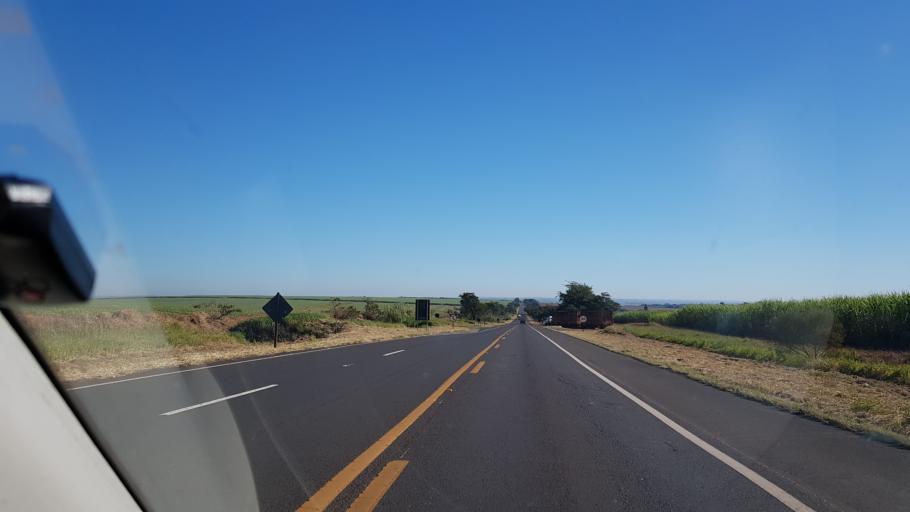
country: BR
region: Sao Paulo
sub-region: Assis
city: Assis
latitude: -22.5642
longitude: -50.5240
